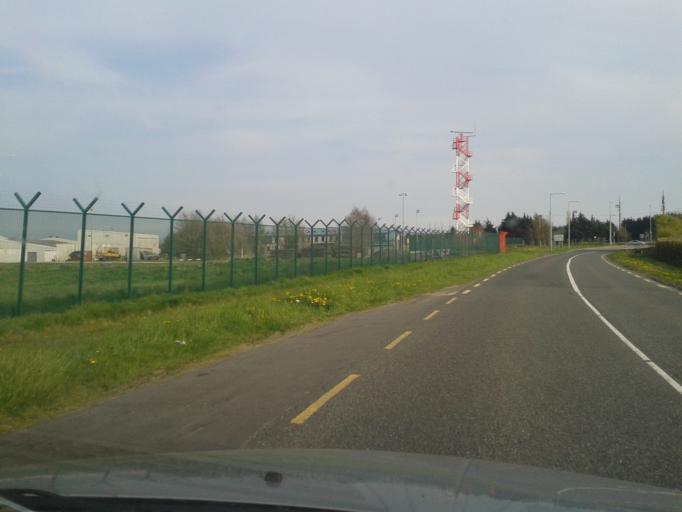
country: IE
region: Leinster
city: Ballymun
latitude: 53.4187
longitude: -6.2679
